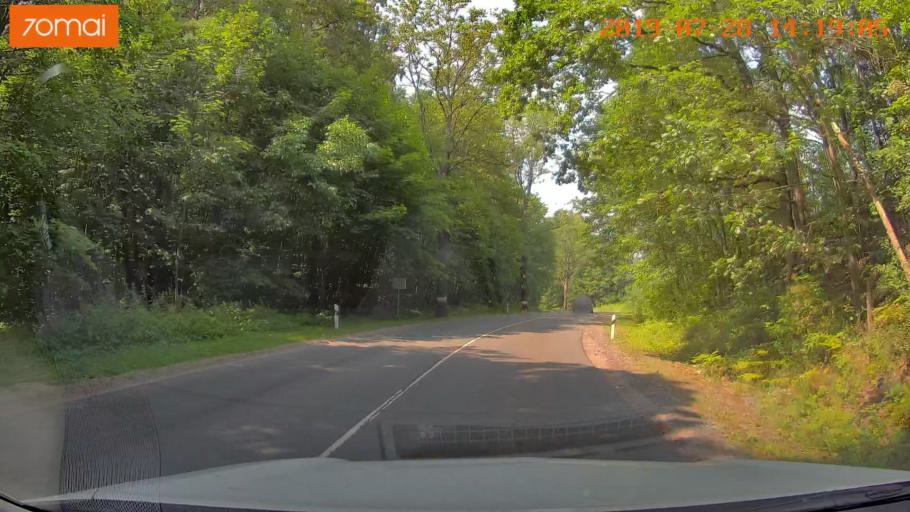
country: RU
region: Kaliningrad
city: Volochayevskoye
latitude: 54.8180
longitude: 20.2310
